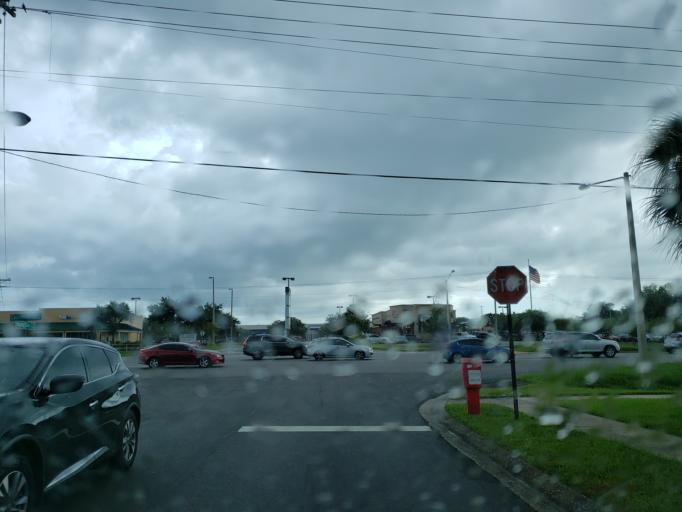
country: US
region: Florida
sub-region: Hillsborough County
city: Brandon
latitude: 27.9237
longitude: -82.3209
